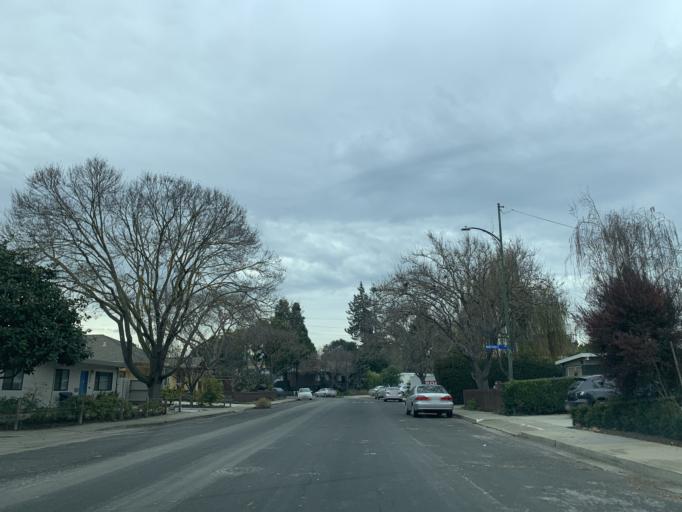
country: US
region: California
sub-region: Santa Clara County
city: Mountain View
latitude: 37.4037
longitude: -122.0672
